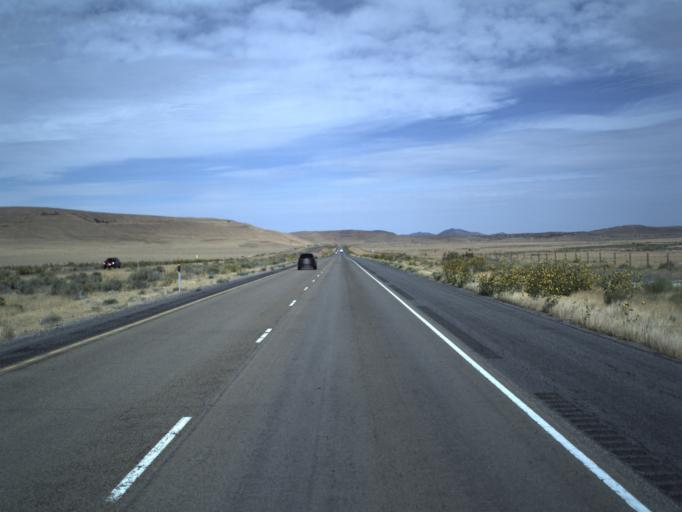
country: US
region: Utah
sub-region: Tooele County
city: Grantsville
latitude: 40.7999
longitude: -112.8488
